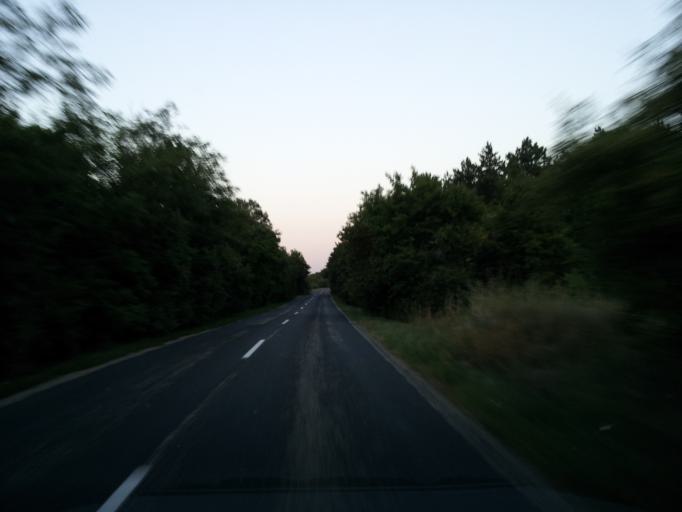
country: HU
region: Fejer
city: Szarliget
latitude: 47.5102
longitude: 18.5467
